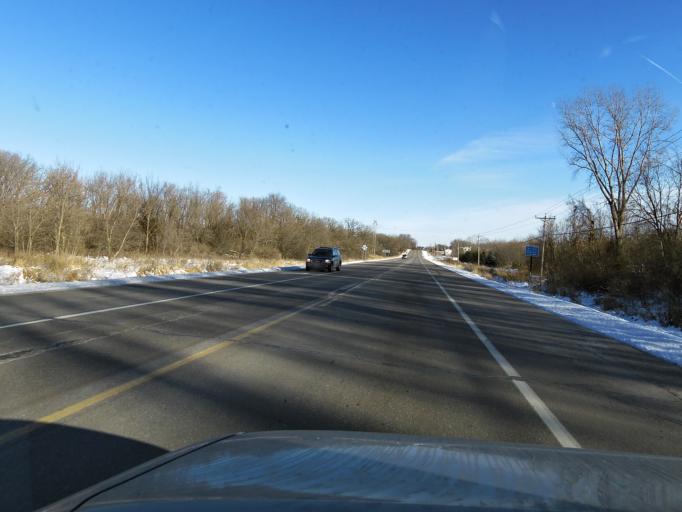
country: US
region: Minnesota
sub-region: Washington County
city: Oakdale
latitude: 44.9914
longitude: -92.9435
